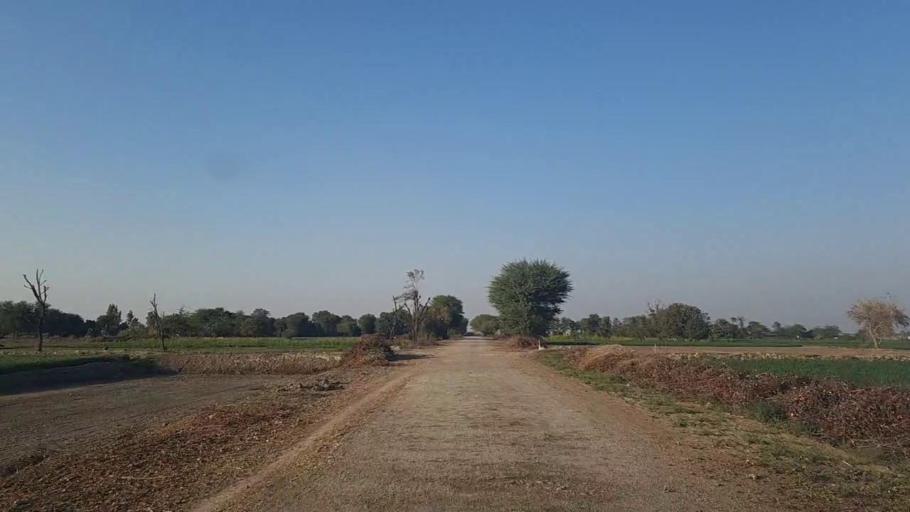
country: PK
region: Sindh
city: Jam Sahib
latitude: 26.3049
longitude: 68.6704
